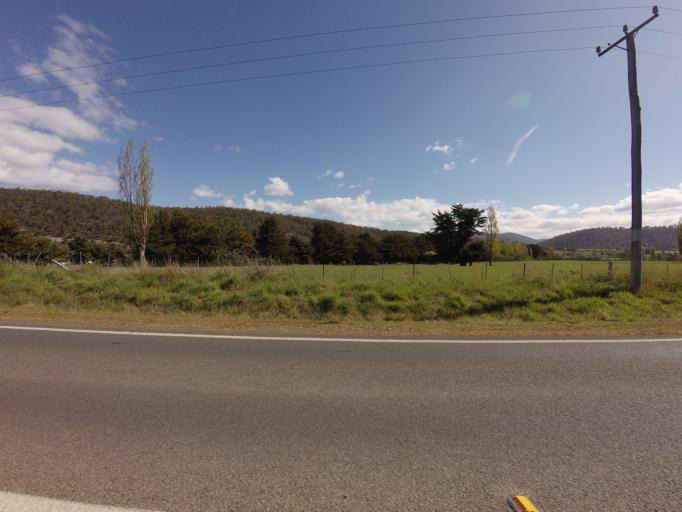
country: AU
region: Tasmania
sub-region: Derwent Valley
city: New Norfolk
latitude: -42.7764
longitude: 147.0378
